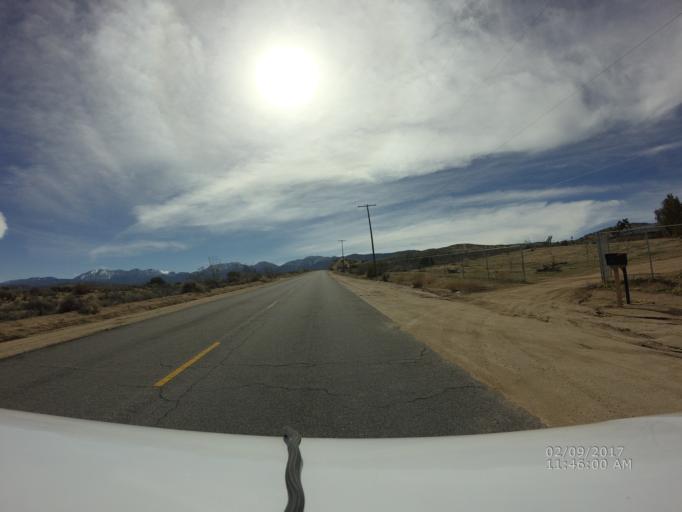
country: US
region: California
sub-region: Los Angeles County
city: Littlerock
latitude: 34.4997
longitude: -117.9141
